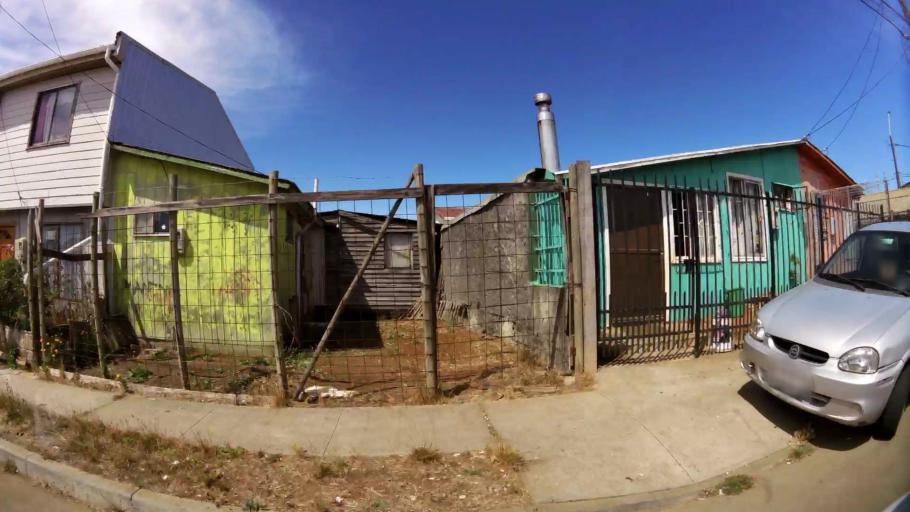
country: CL
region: Biobio
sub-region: Provincia de Concepcion
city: Talcahuano
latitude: -36.7096
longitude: -73.1200
